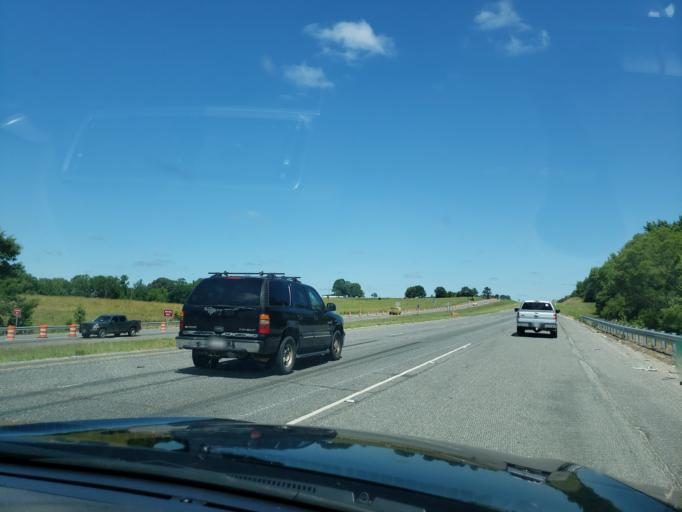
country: US
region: Alabama
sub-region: Lee County
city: Auburn
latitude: 32.6811
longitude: -85.4910
